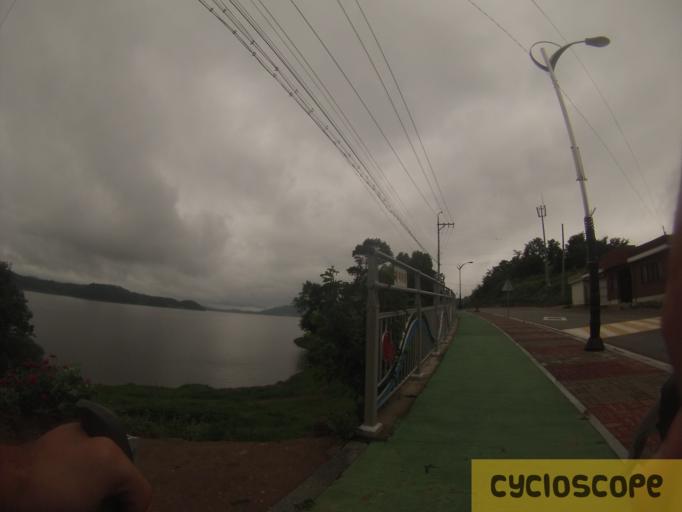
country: KR
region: Chungcheongnam-do
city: Yesan
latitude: 36.7474
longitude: 126.8690
